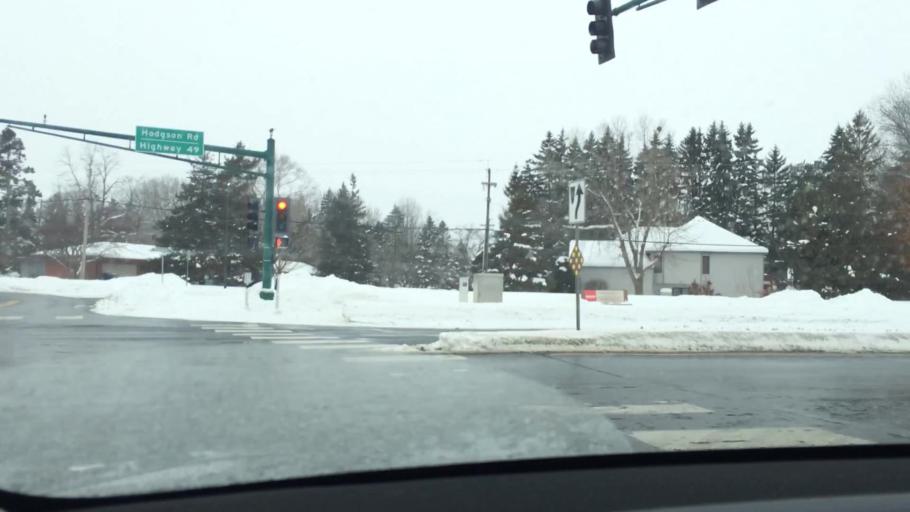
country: US
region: Minnesota
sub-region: Ramsey County
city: Shoreview
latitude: 45.0911
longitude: -93.1264
